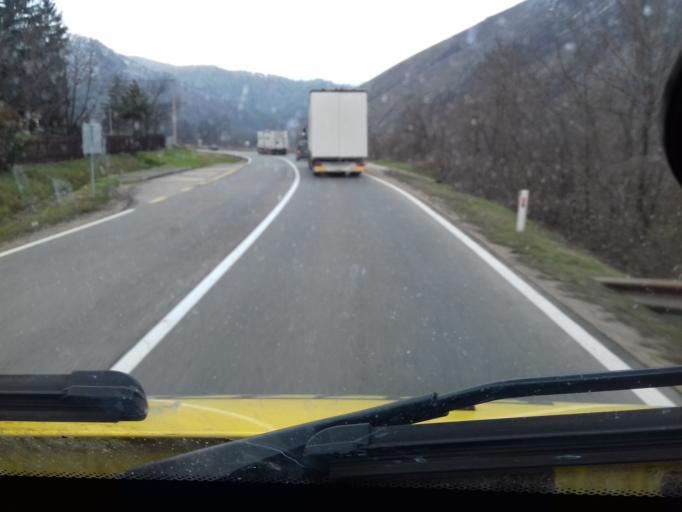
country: BA
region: Federation of Bosnia and Herzegovina
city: Zepce
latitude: 44.4050
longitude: 18.0057
